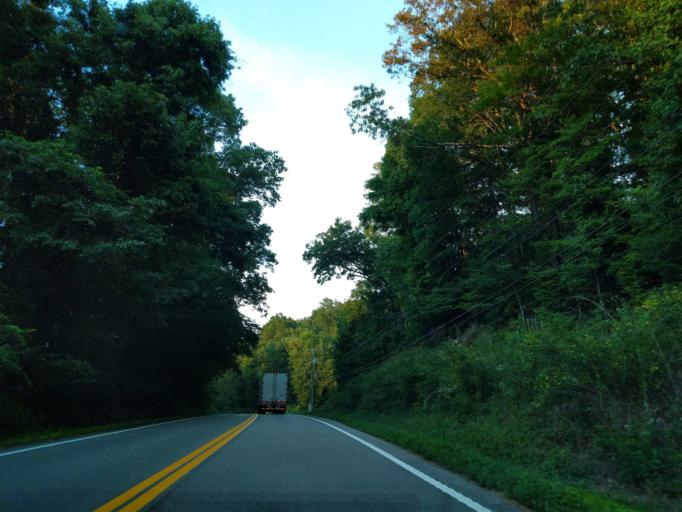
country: US
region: Georgia
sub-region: Walker County
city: Lookout Mountain
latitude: 35.0250
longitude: -85.4364
